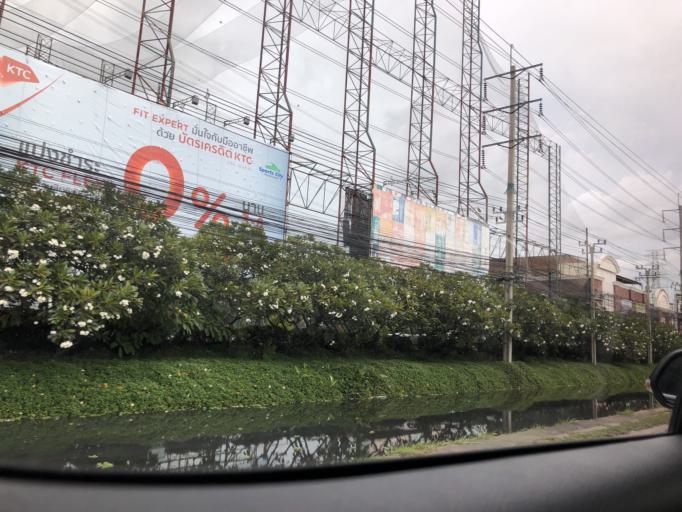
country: TH
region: Bangkok
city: Lak Si
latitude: 13.8785
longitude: 100.5502
